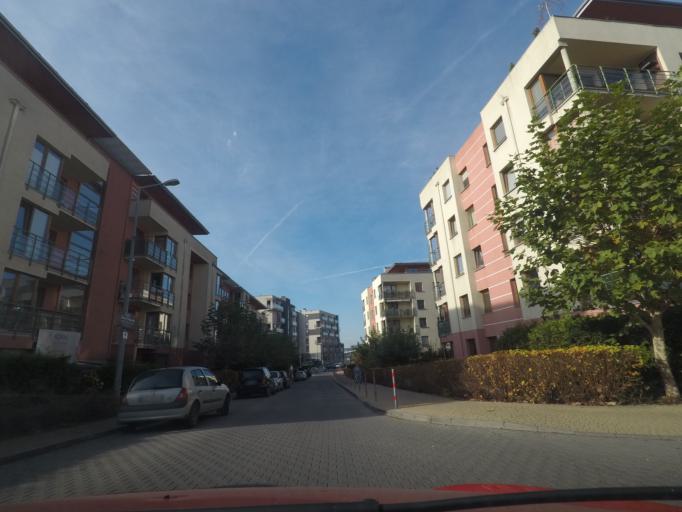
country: PL
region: Lesser Poland Voivodeship
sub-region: Krakow
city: Sidzina
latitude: 50.0203
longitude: 19.9014
